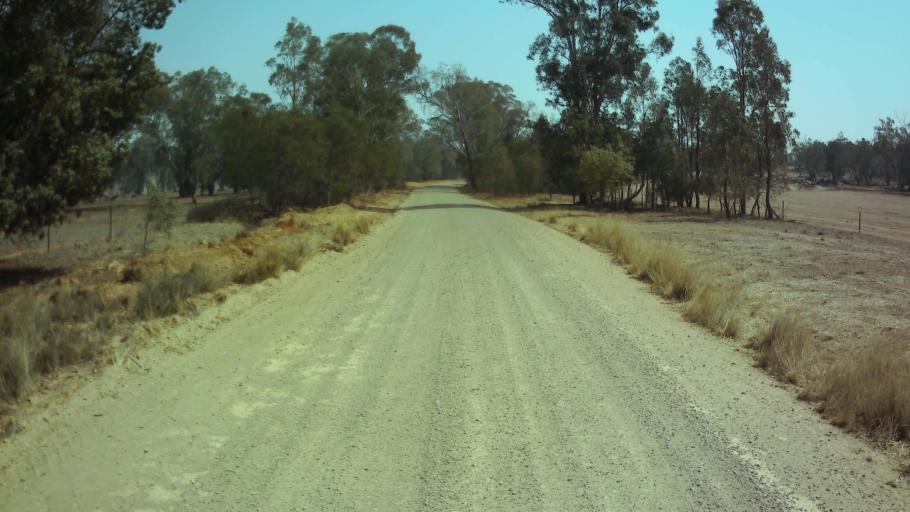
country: AU
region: New South Wales
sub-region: Weddin
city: Grenfell
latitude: -33.6665
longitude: 148.2745
